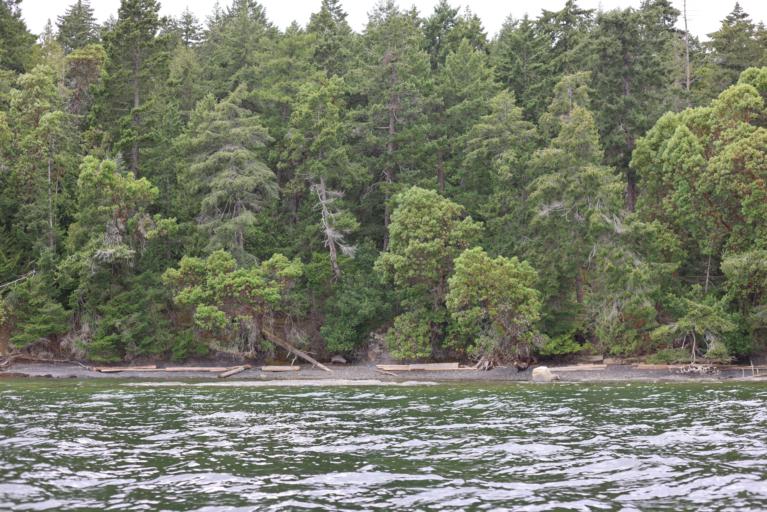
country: CA
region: British Columbia
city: North Cowichan
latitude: 48.9013
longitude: -123.6637
